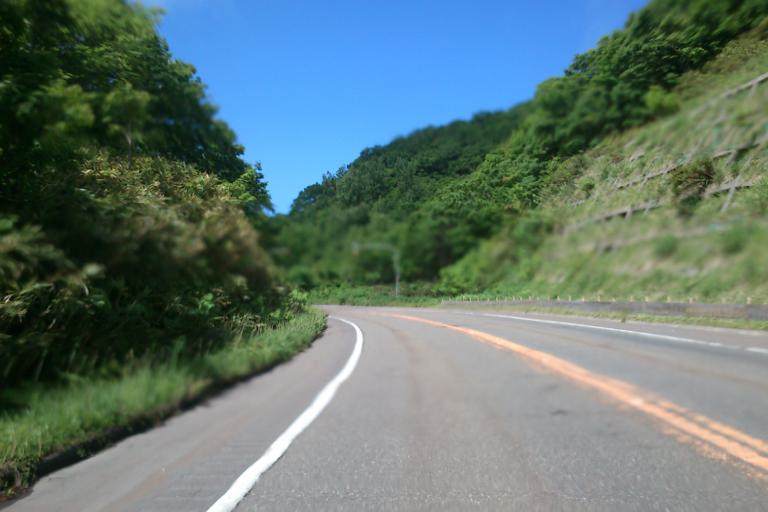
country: JP
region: Hokkaido
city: Ishikari
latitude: 43.4813
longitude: 141.3952
